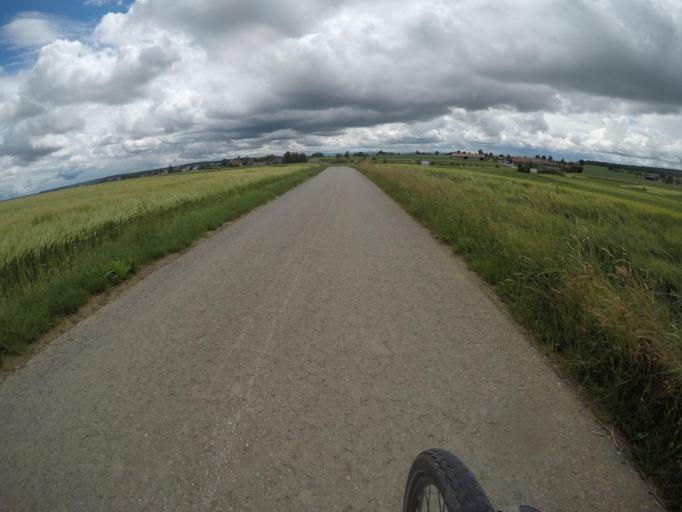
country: DE
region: Baden-Wuerttemberg
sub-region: Regierungsbezirk Stuttgart
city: Deckenpfronn
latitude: 48.6152
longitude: 8.8272
